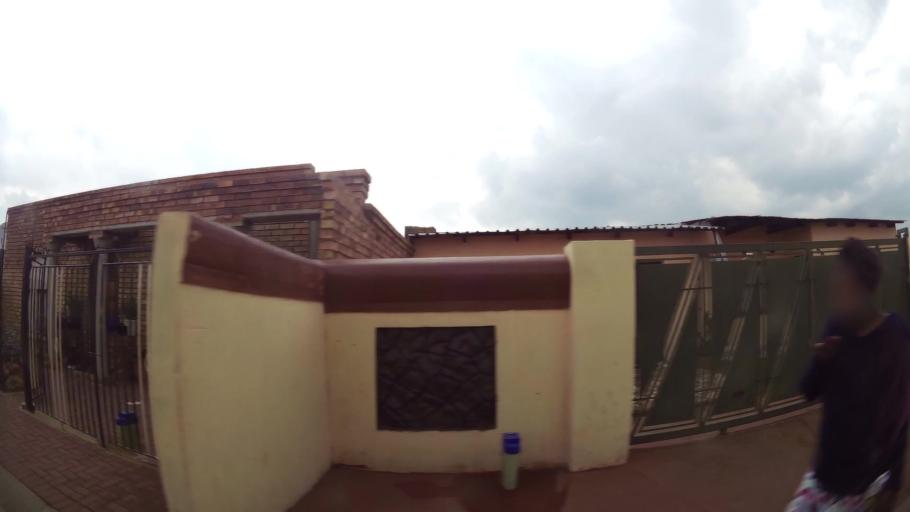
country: ZA
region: Gauteng
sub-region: Ekurhuleni Metropolitan Municipality
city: Germiston
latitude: -26.3687
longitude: 28.1602
